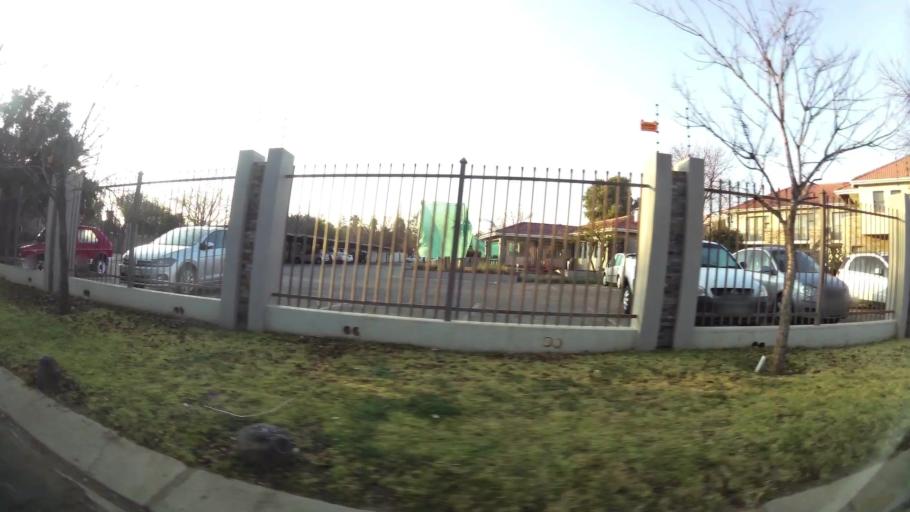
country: ZA
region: Orange Free State
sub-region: Mangaung Metropolitan Municipality
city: Bloemfontein
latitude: -29.0860
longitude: 26.1555
